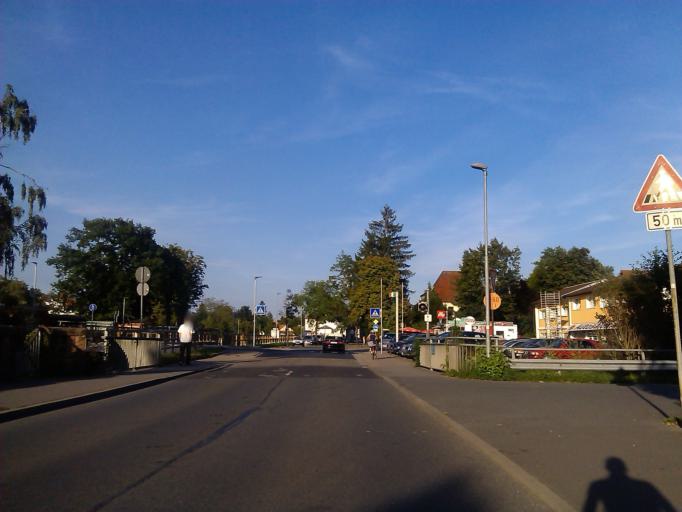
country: DE
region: Baden-Wuerttemberg
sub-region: Karlsruhe Region
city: Wiesloch
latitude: 49.2914
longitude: 8.6848
